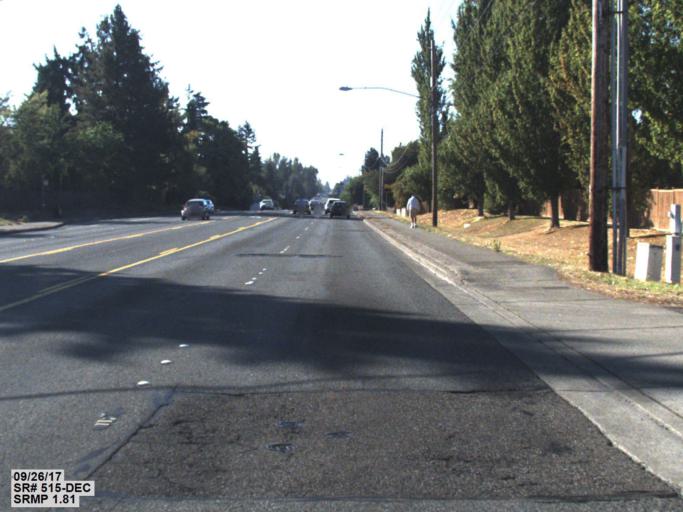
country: US
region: Washington
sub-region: King County
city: East Hill-Meridian
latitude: 47.3987
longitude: -122.2022
